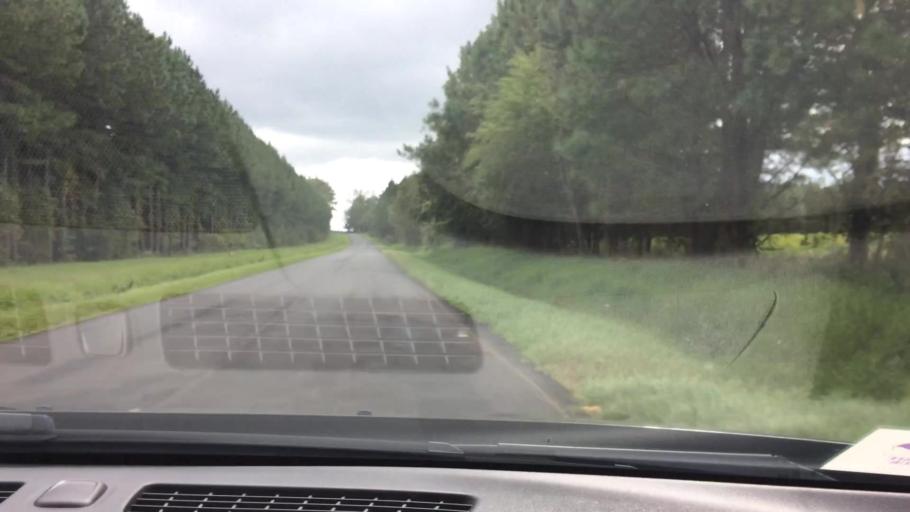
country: US
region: North Carolina
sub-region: Greene County
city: Maury
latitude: 35.5288
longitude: -77.5443
